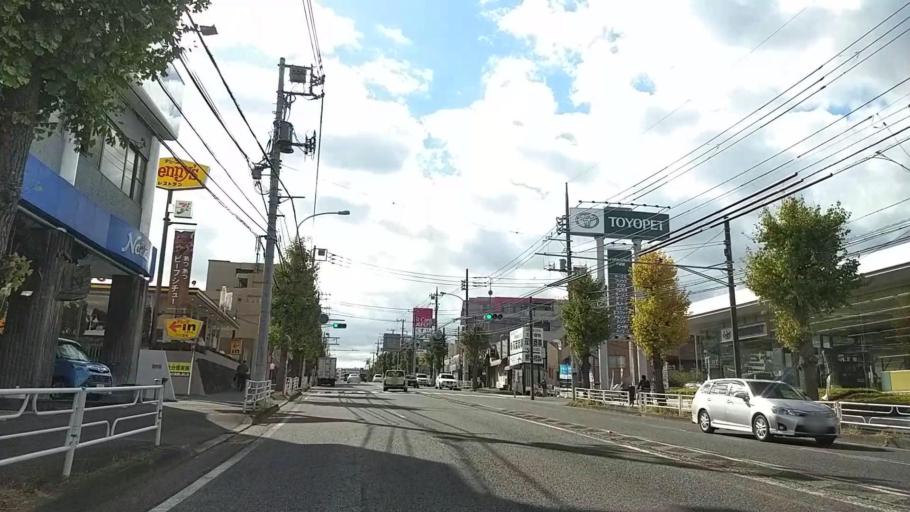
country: JP
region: Kanagawa
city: Yokohama
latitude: 35.4886
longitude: 139.6053
